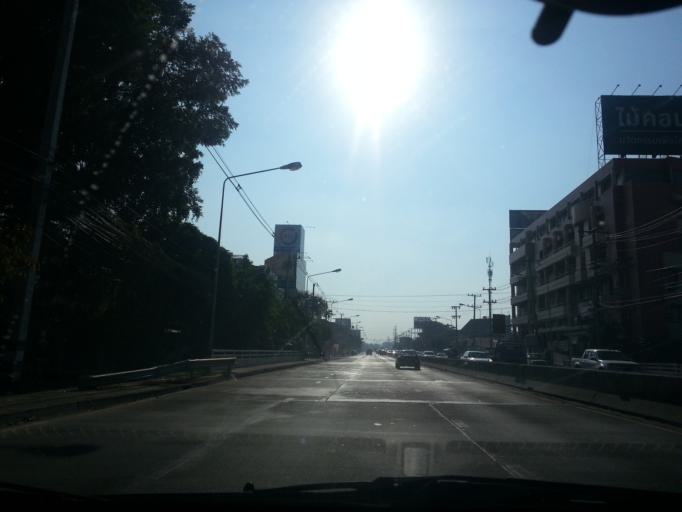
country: TH
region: Chiang Mai
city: Chiang Mai
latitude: 18.7635
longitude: 98.9933
